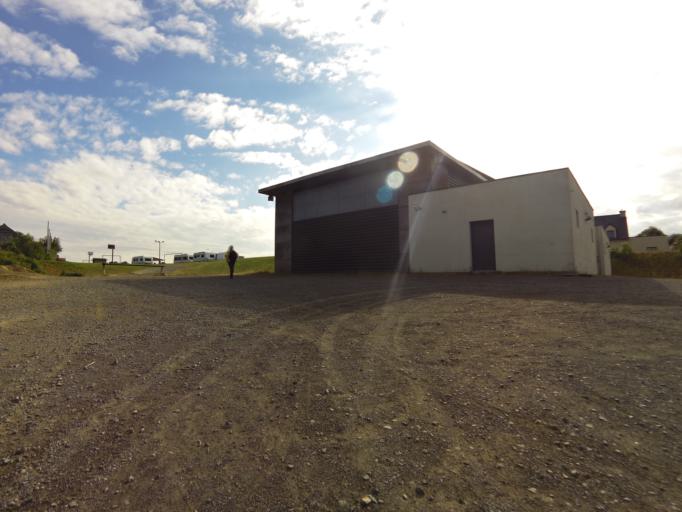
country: FR
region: Brittany
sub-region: Departement d'Ille-et-Vilaine
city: Saint-Medard-sur-Ille
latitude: 48.2520
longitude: -1.6571
